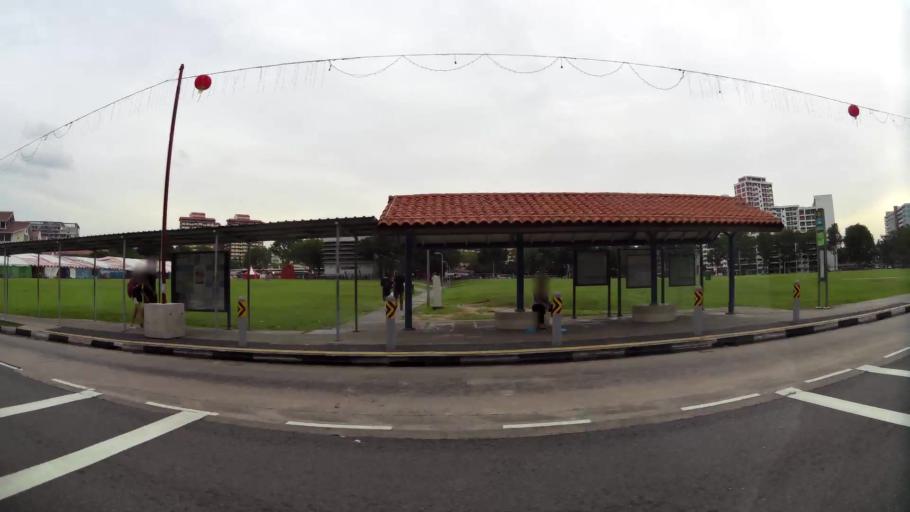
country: SG
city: Singapore
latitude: 1.3730
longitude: 103.8918
